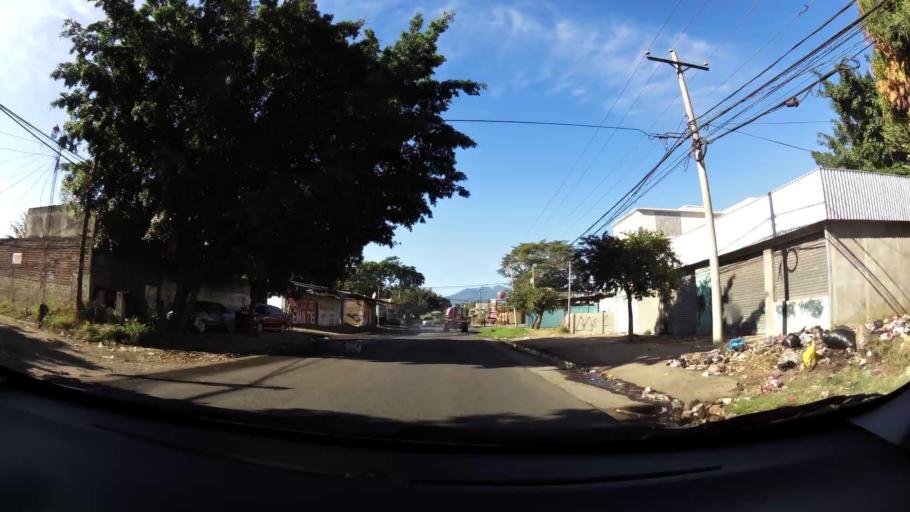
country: SV
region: Santa Ana
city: Santa Ana
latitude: 13.9771
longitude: -89.5815
